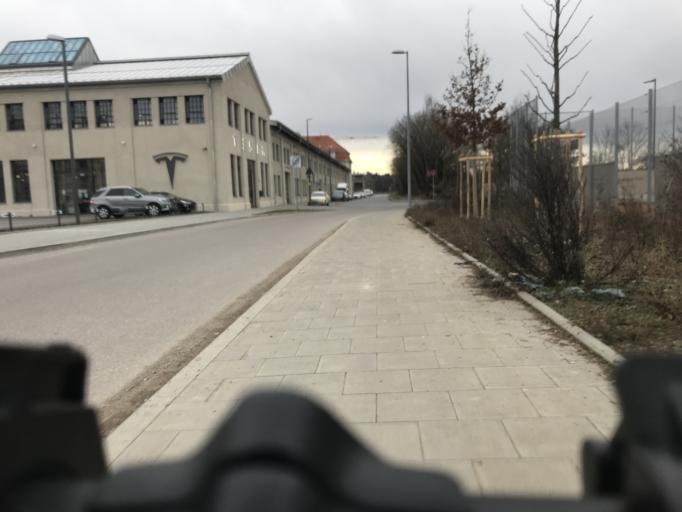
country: DE
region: Bavaria
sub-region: Upper Bavaria
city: Grafelfing
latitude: 48.1385
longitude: 11.4176
